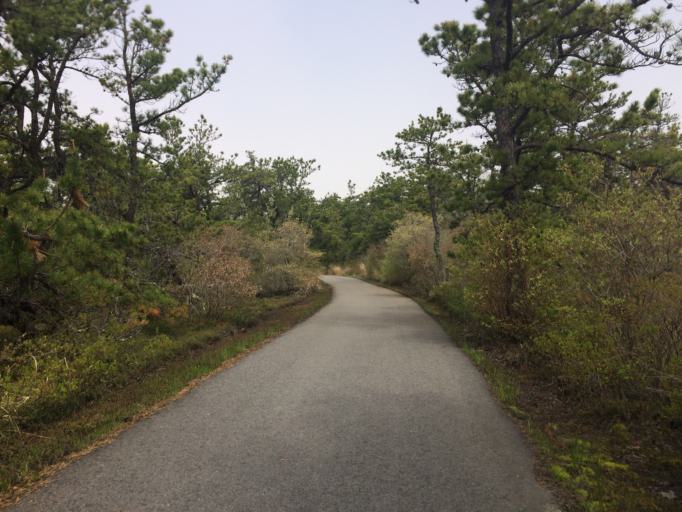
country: US
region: Massachusetts
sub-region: Barnstable County
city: Provincetown
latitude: 42.0752
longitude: -70.2092
